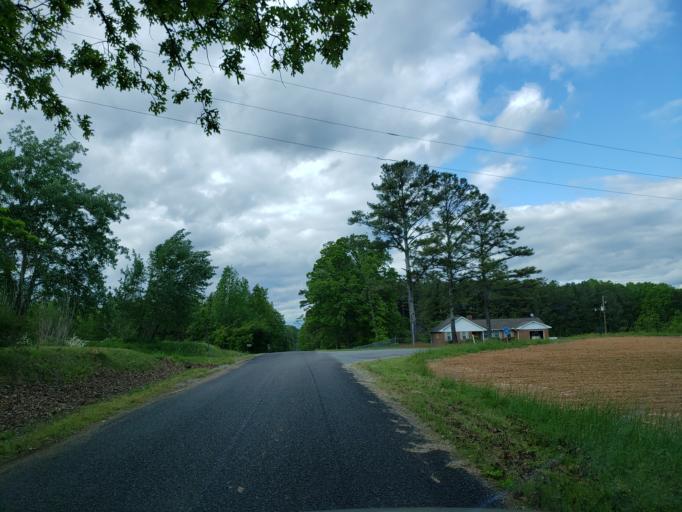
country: US
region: Georgia
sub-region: Haralson County
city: Tallapoosa
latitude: 33.8154
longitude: -85.3865
